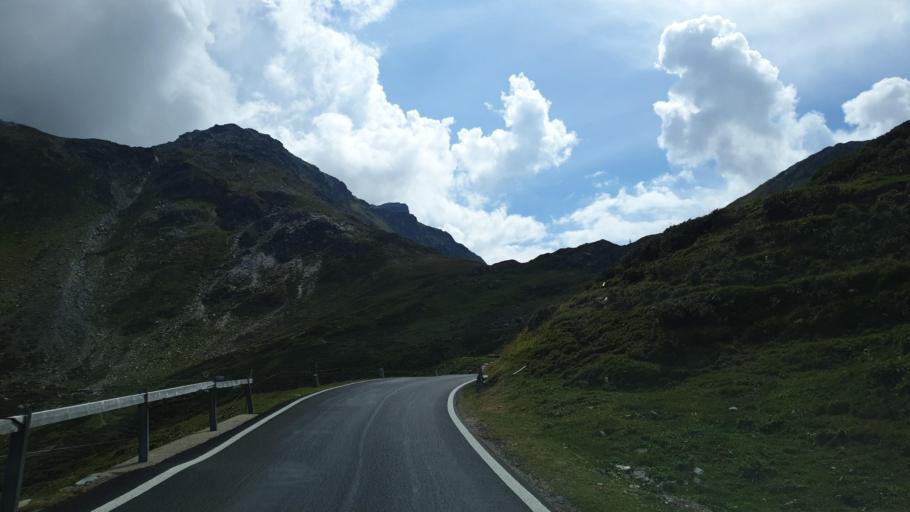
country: IT
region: Lombardy
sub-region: Provincia di Sondrio
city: Campodolcino
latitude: 46.5134
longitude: 9.3288
